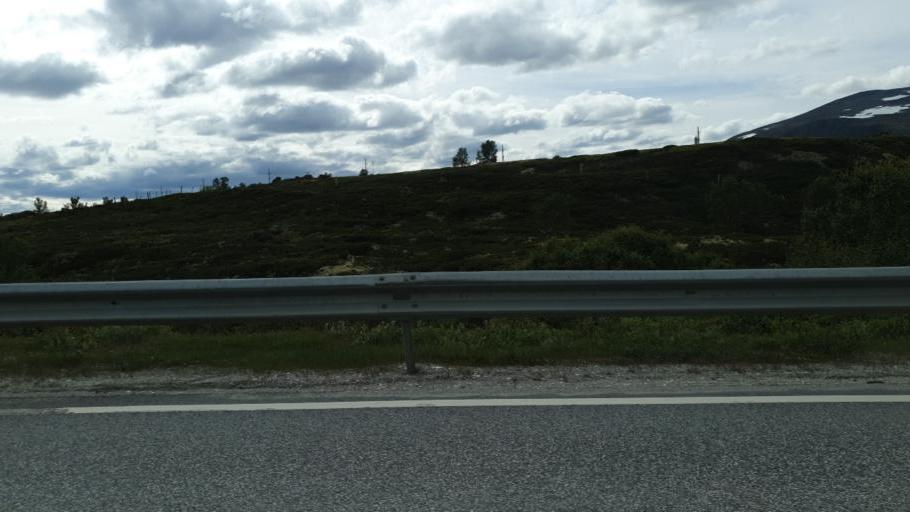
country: NO
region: Sor-Trondelag
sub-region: Oppdal
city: Oppdal
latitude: 62.2692
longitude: 9.5837
